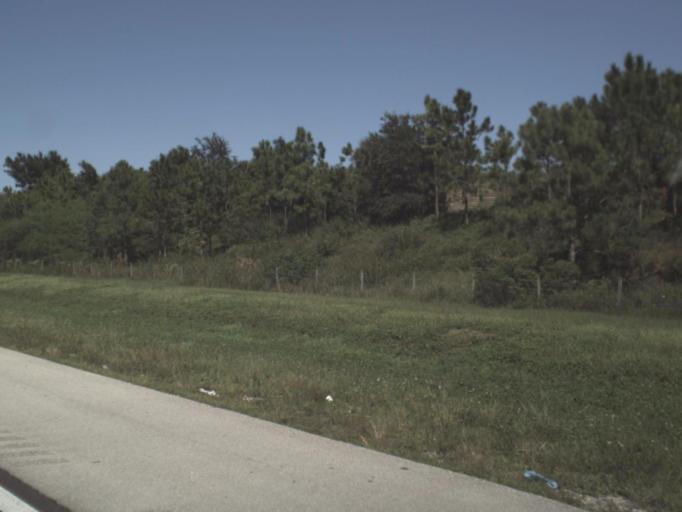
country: US
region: Florida
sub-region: Lee County
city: Gateway
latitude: 26.5925
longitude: -81.7971
